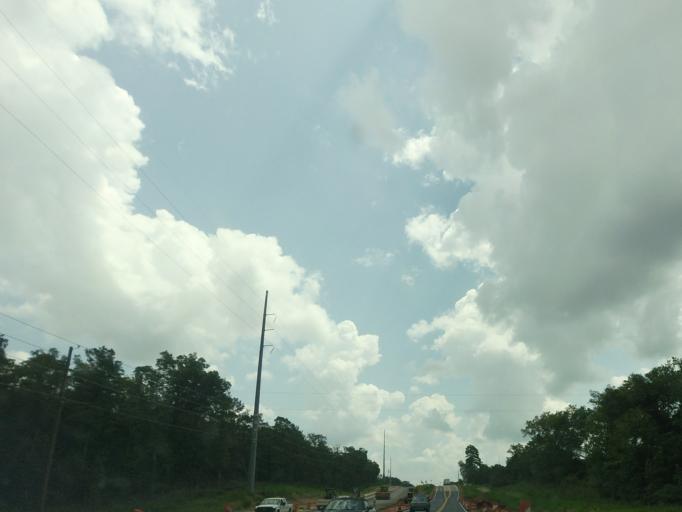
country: US
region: Georgia
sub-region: Houston County
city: Perry
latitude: 32.5464
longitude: -83.7244
